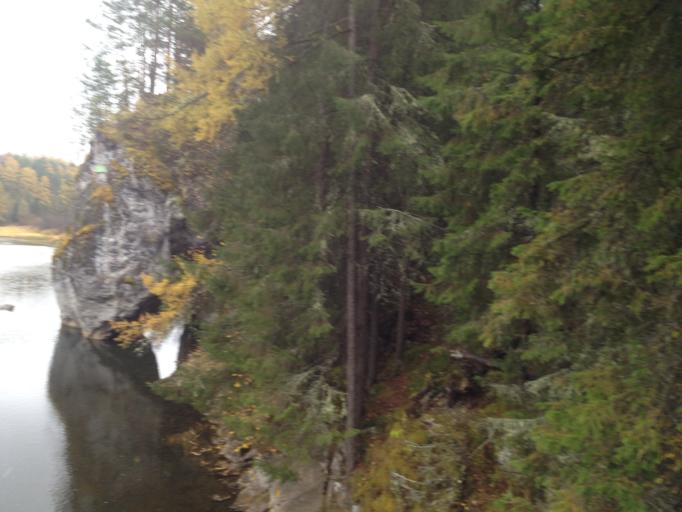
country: RU
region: Sverdlovsk
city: Mikhaylovsk
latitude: 56.5118
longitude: 59.2555
